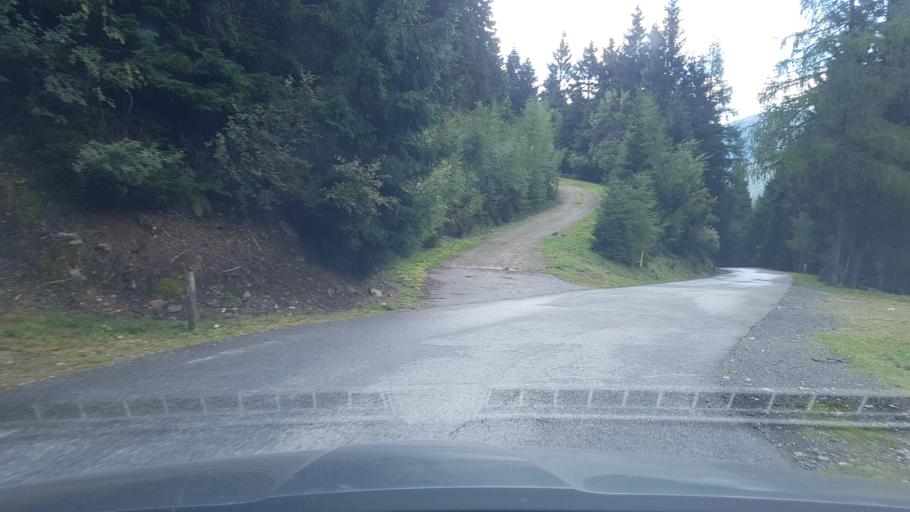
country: AT
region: Styria
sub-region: Politischer Bezirk Liezen
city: Sankt Nikolai im Solktal
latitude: 47.2555
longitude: 14.0816
